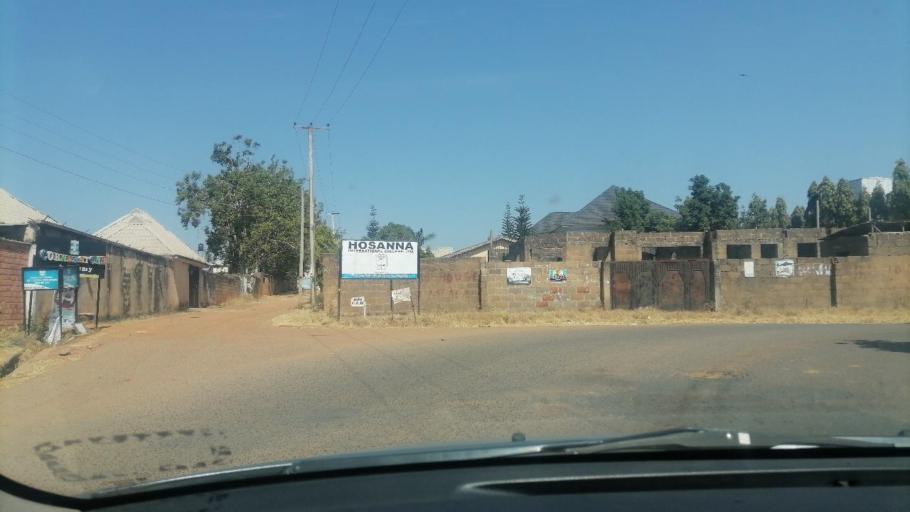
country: NG
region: Plateau
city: Jos
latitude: 9.8671
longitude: 8.9062
